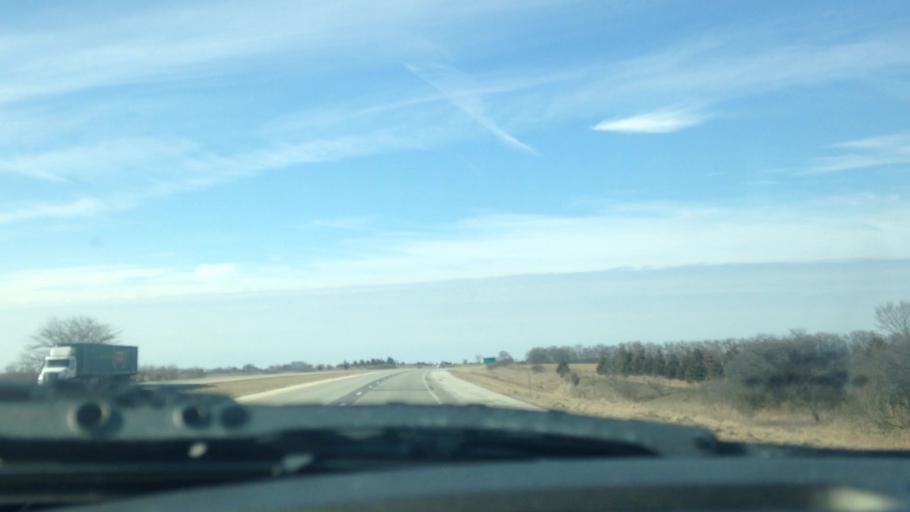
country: US
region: Illinois
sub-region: Ford County
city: Paxton
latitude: 40.5453
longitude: -88.0646
